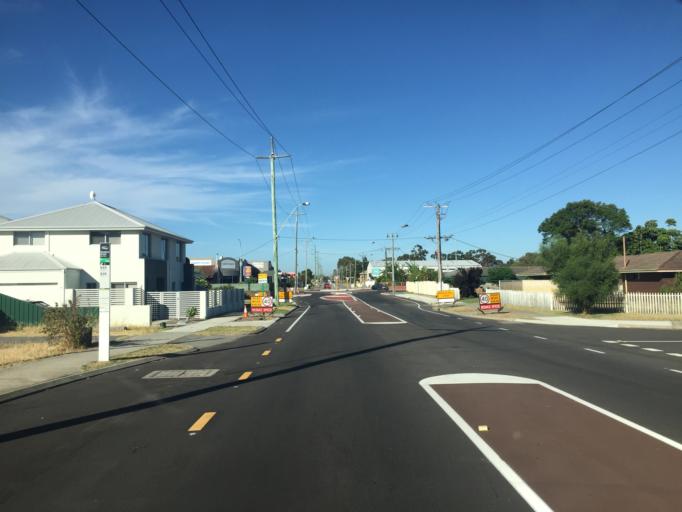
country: AU
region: Western Australia
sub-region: Belmont
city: Rivervale
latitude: -31.9620
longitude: 115.9272
